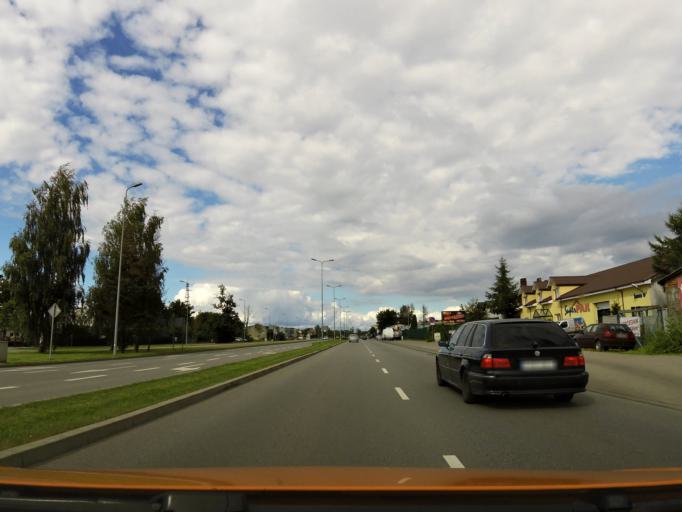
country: PL
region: West Pomeranian Voivodeship
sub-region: Powiat kolobrzeski
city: Kolobrzeg
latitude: 54.1688
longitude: 15.5540
